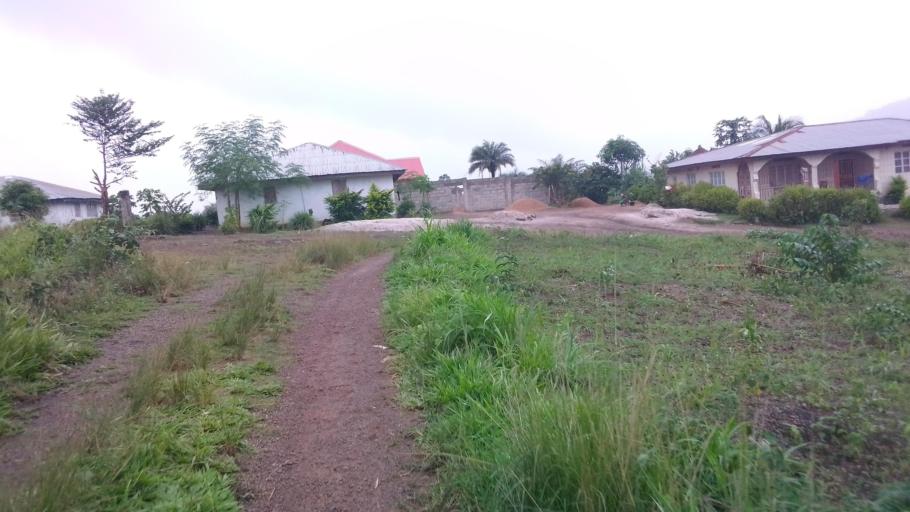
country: SL
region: Eastern Province
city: Kenema
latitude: 7.8353
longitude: -11.2136
